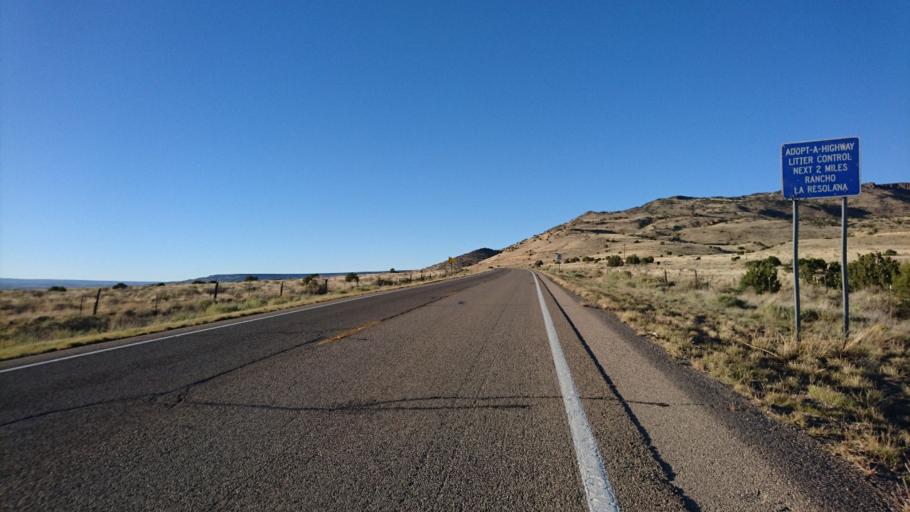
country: US
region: New Mexico
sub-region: Cibola County
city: Grants
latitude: 35.1098
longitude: -107.7815
